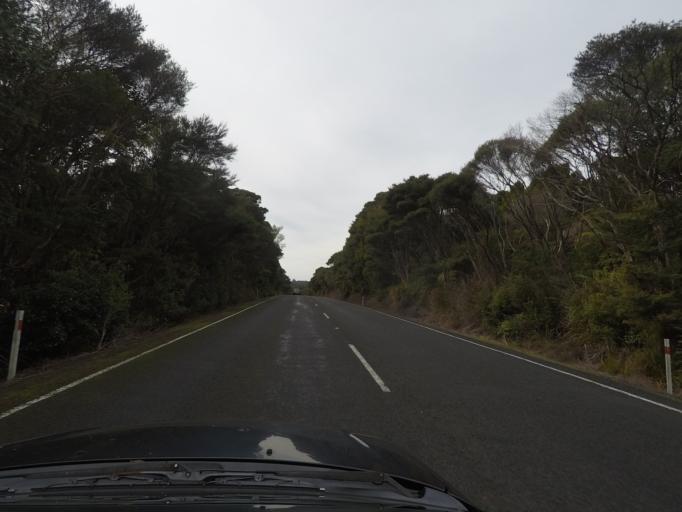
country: NZ
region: Auckland
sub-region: Auckland
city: Titirangi
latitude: -36.9433
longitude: 174.5493
